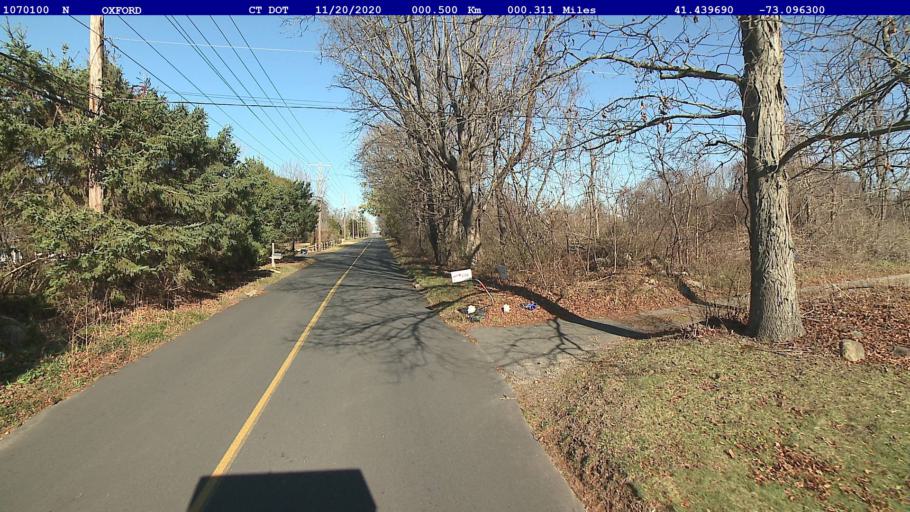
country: US
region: Connecticut
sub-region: New Haven County
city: Oxford
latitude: 41.4397
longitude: -73.0963
